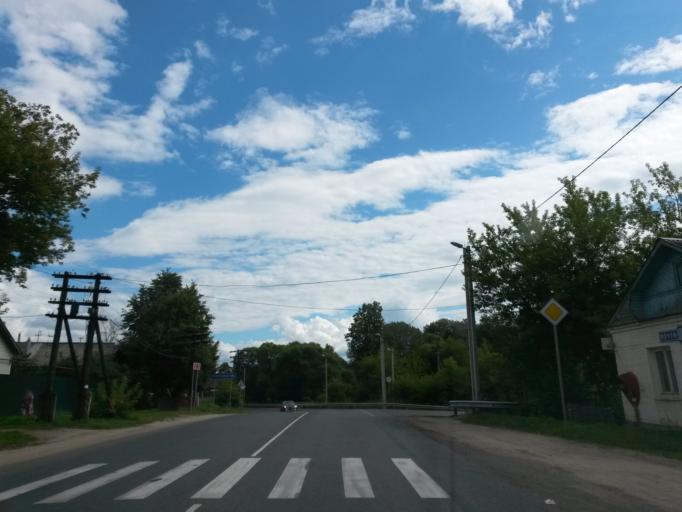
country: RU
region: Ivanovo
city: Novo-Talitsy
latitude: 57.0648
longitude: 40.7065
